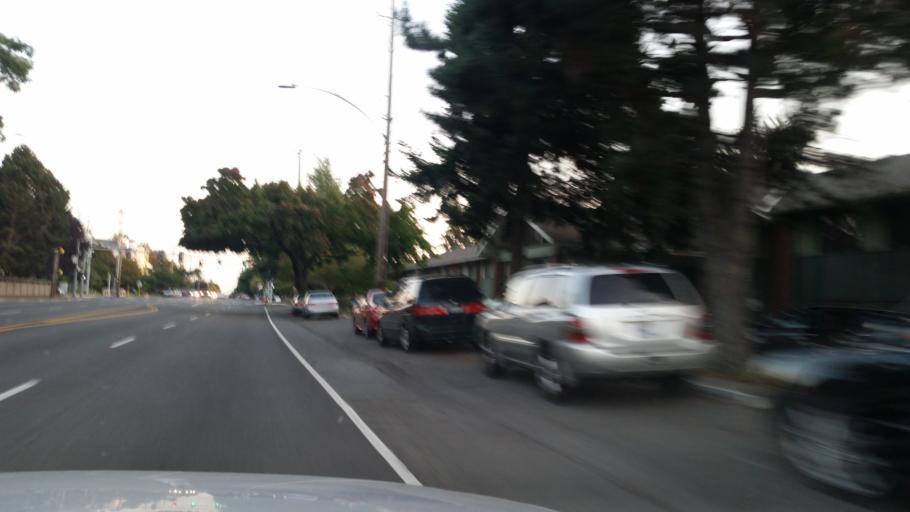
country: US
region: Washington
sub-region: King County
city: Shoreline
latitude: 47.7243
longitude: -122.3556
